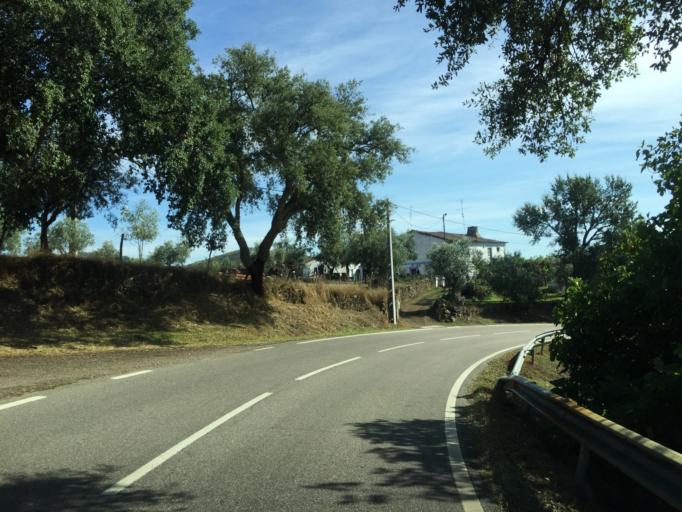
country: PT
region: Portalegre
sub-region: Marvao
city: Marvao
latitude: 39.3918
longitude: -7.3885
